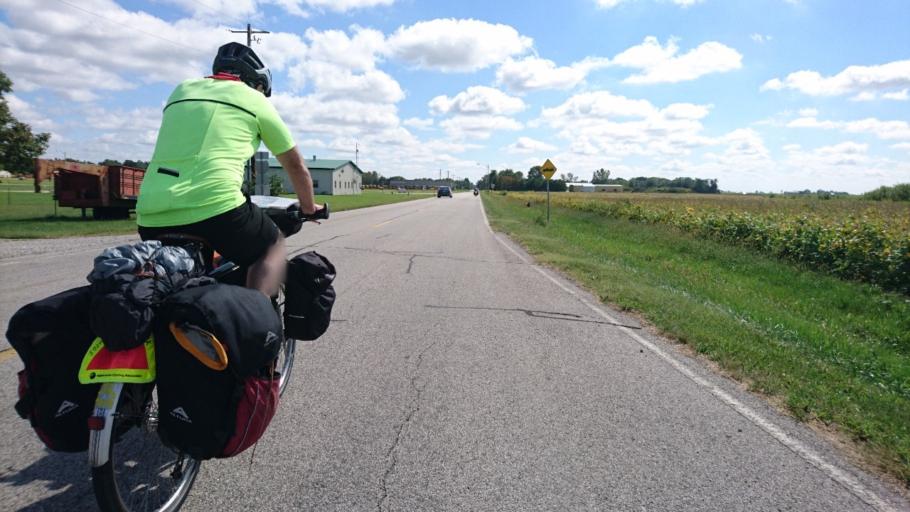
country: US
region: Illinois
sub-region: Montgomery County
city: Litchfield
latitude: 39.1612
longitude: -89.6665
